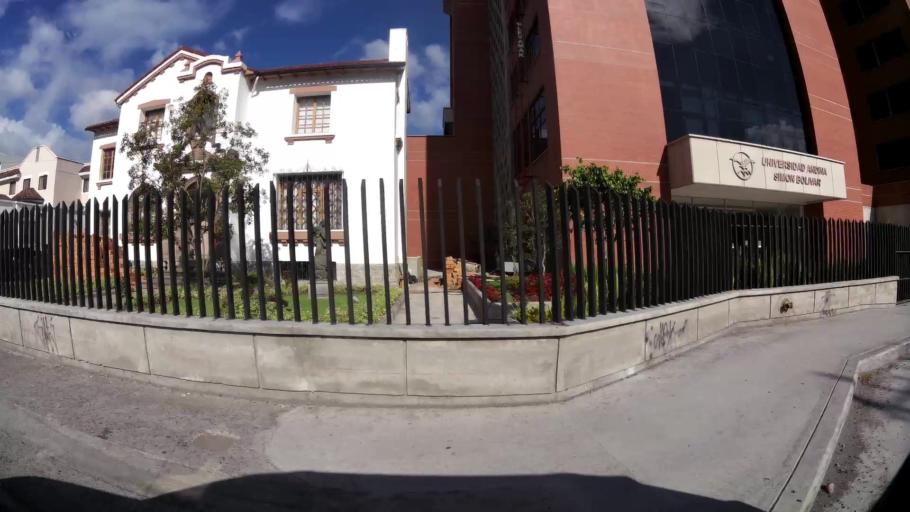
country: EC
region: Pichincha
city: Quito
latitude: -0.2107
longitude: -78.4874
